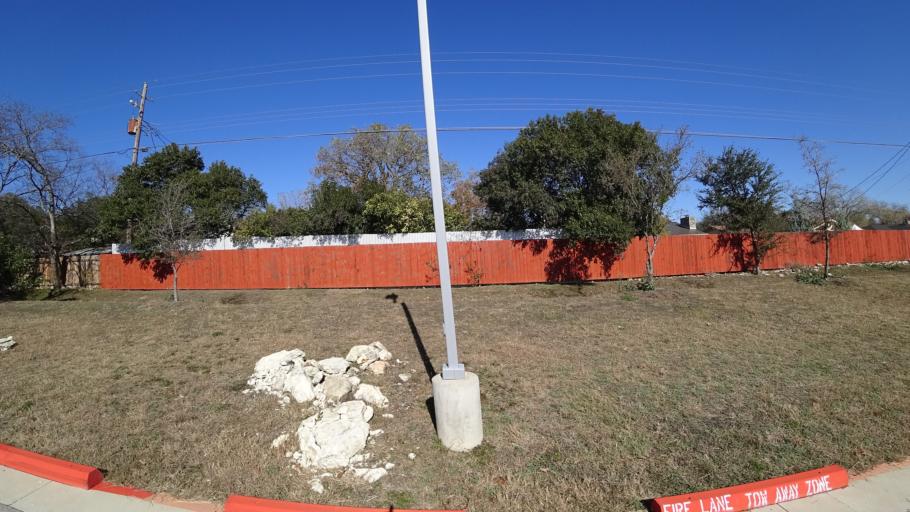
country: US
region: Texas
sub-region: Travis County
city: Wells Branch
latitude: 30.4252
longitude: -97.6996
